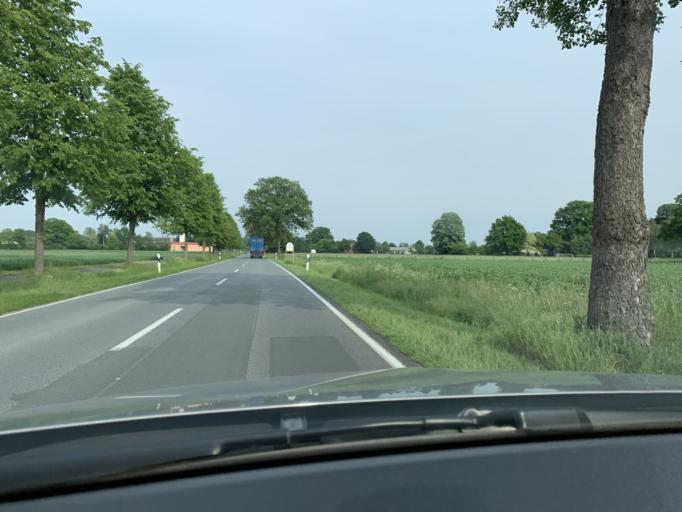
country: DE
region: North Rhine-Westphalia
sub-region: Regierungsbezirk Detmold
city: Langenberg
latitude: 51.7726
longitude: 8.3677
